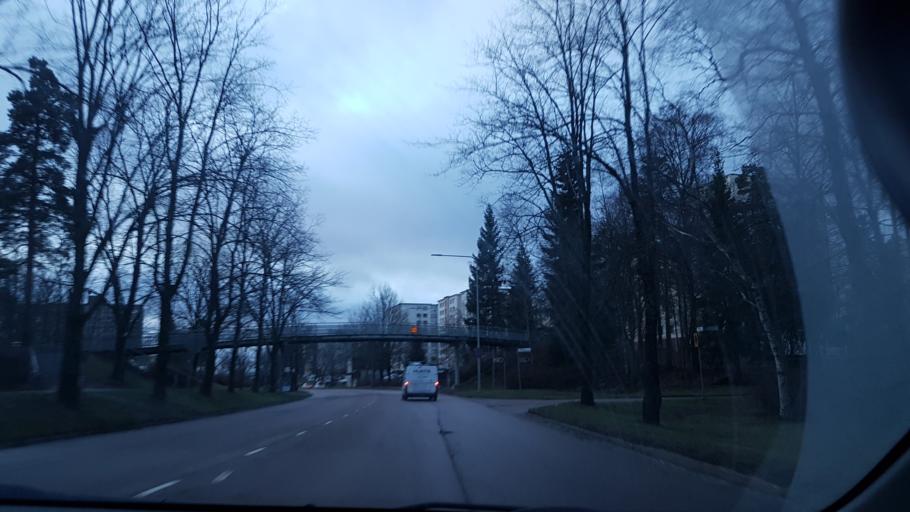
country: FI
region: Uusimaa
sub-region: Helsinki
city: Vantaa
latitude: 60.2771
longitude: 25.1048
